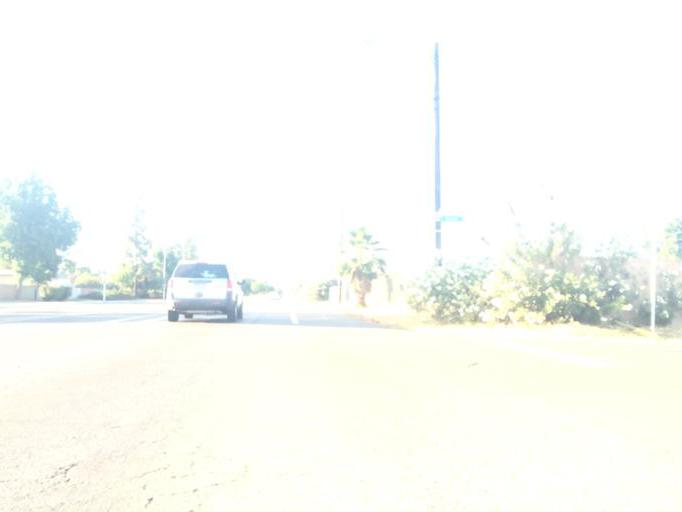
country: US
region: California
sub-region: Fresno County
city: Tarpey Village
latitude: 36.7866
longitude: -119.6821
